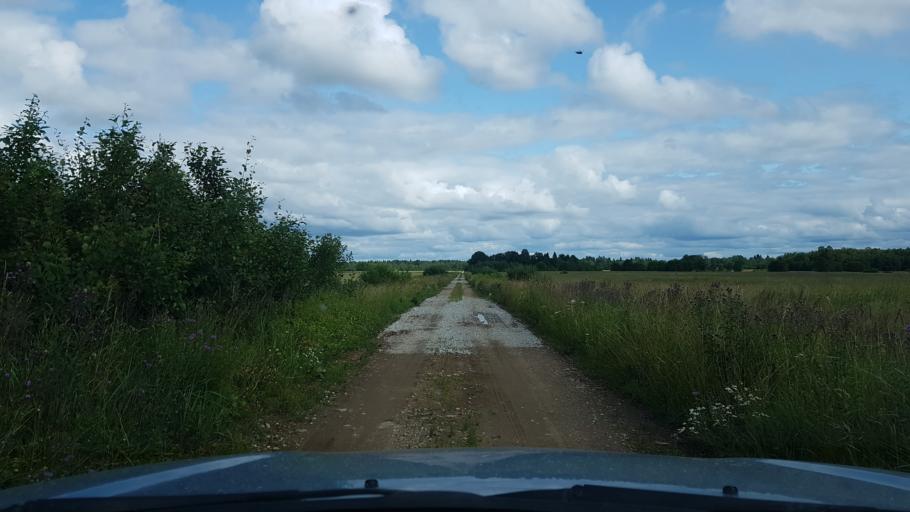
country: EE
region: Ida-Virumaa
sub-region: Narva-Joesuu linn
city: Narva-Joesuu
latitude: 59.3701
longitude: 27.9355
